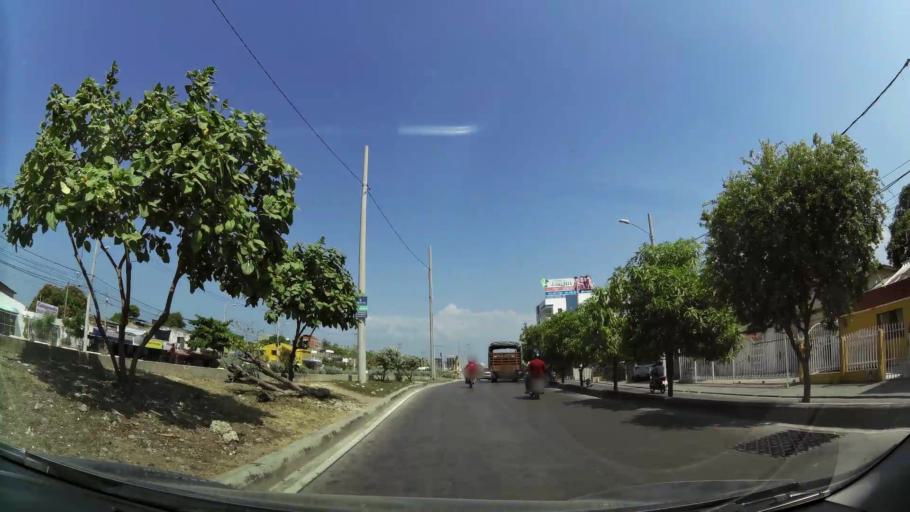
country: CO
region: Bolivar
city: Cartagena
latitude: 10.3961
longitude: -75.4761
